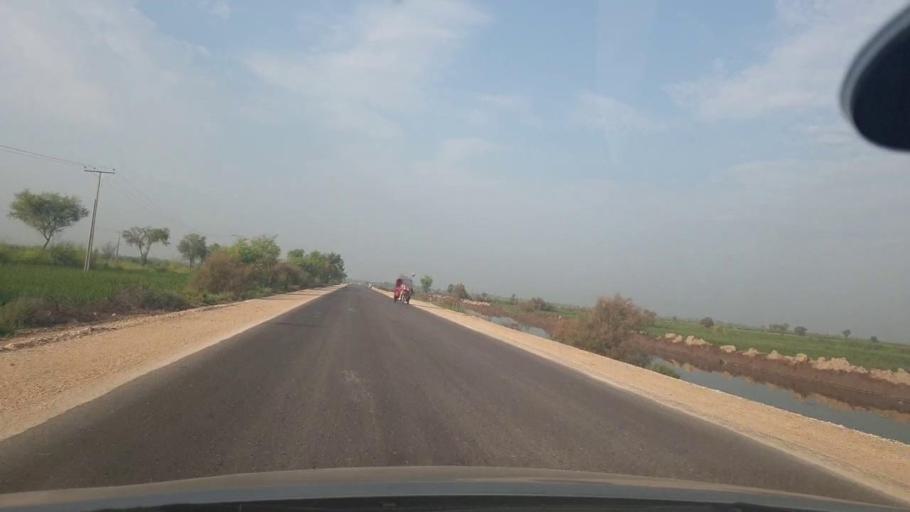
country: PK
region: Sindh
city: Jacobabad
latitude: 28.2281
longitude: 68.3811
